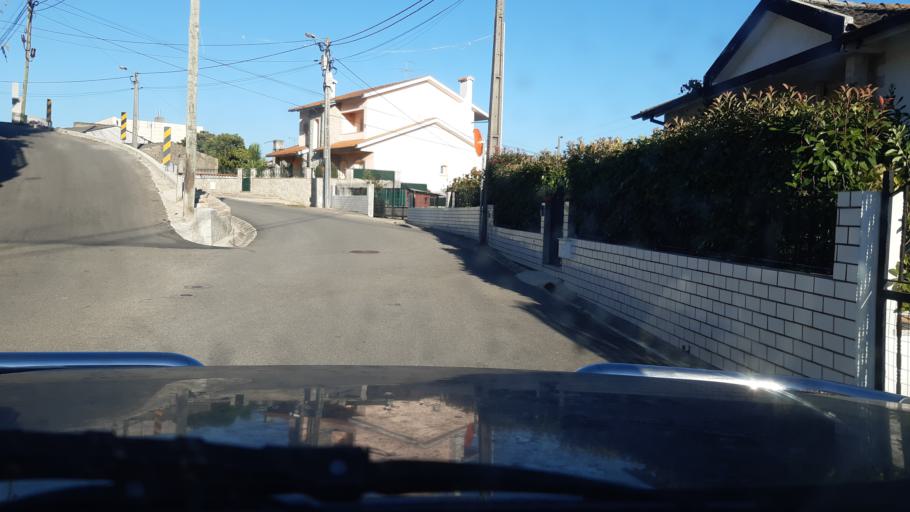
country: PT
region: Aveiro
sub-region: Agueda
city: Agueda
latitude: 40.5748
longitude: -8.4697
